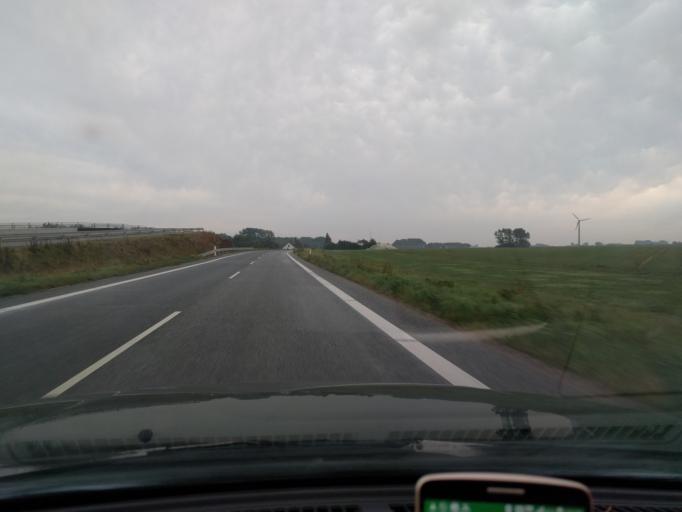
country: DK
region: Zealand
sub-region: Guldborgsund Kommune
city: Norre Alslev
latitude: 54.9338
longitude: 11.8696
